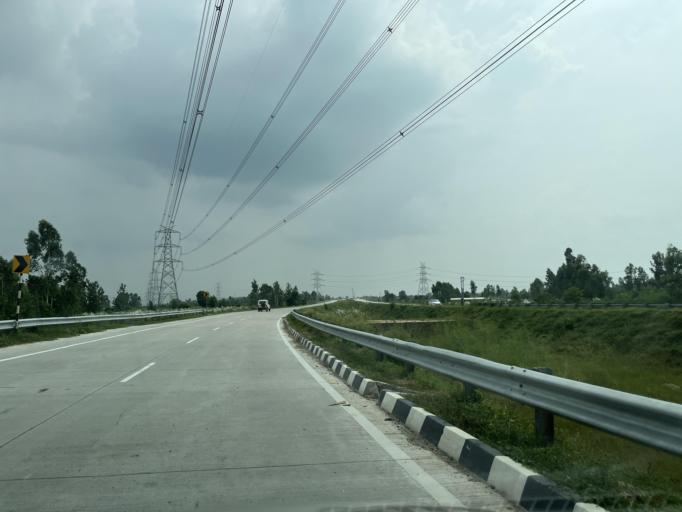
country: IN
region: Uttarakhand
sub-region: Udham Singh Nagar
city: Jaspur
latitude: 29.2775
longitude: 78.8681
